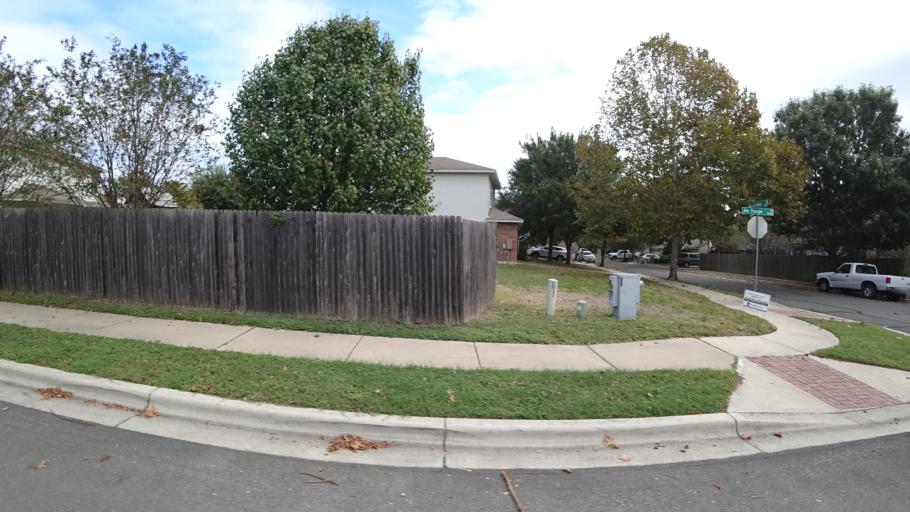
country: US
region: Texas
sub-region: Travis County
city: Manchaca
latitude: 30.1512
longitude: -97.8391
